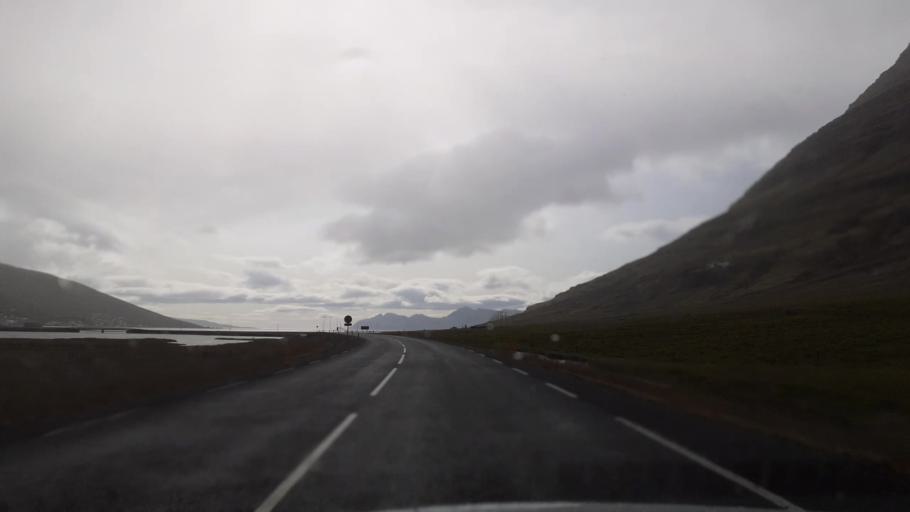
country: IS
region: East
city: Eskifjoerdur
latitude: 65.0778
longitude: -14.0511
